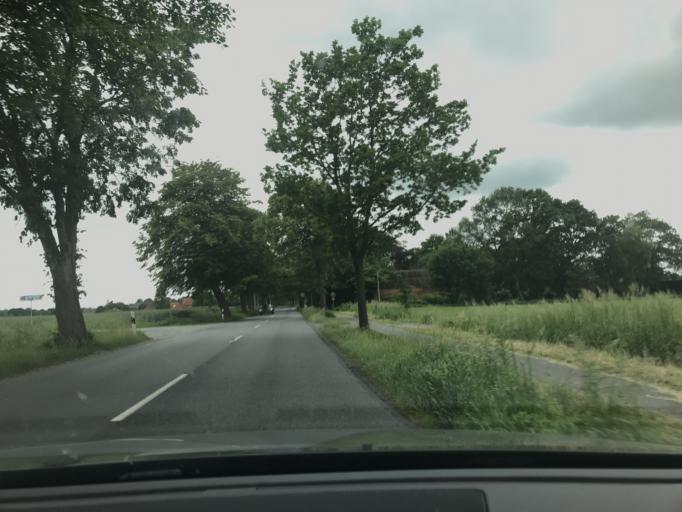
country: DE
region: Lower Saxony
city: Loxstedt
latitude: 53.4615
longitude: 8.6326
